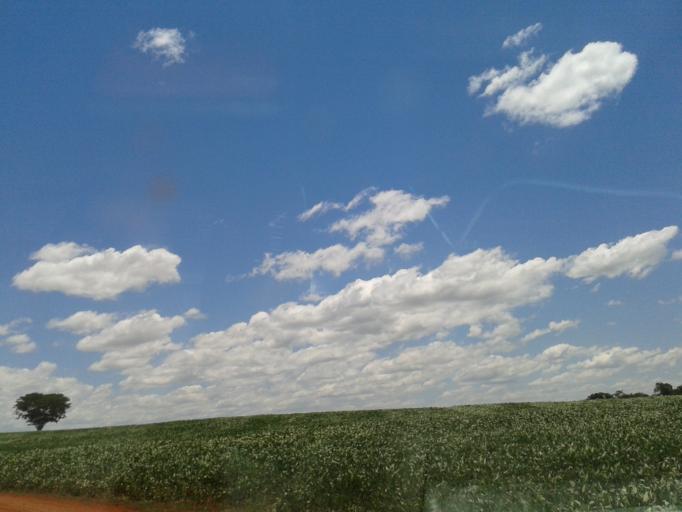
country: BR
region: Minas Gerais
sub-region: Centralina
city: Centralina
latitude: -18.6937
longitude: -49.2197
